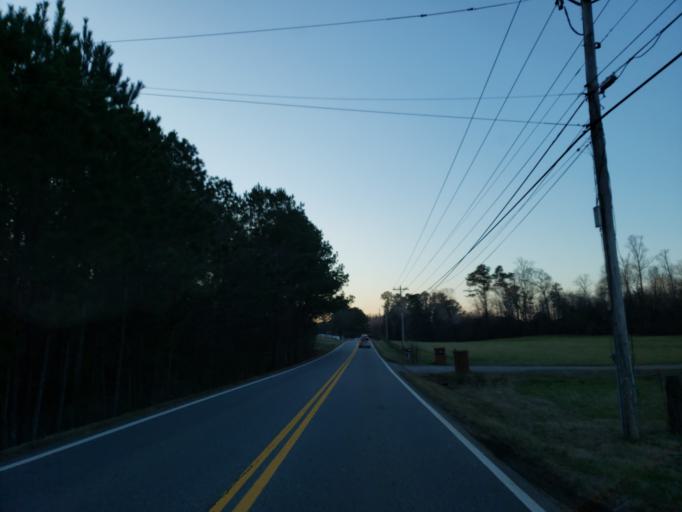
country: US
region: Georgia
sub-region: Cherokee County
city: Woodstock
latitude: 34.1155
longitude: -84.4601
